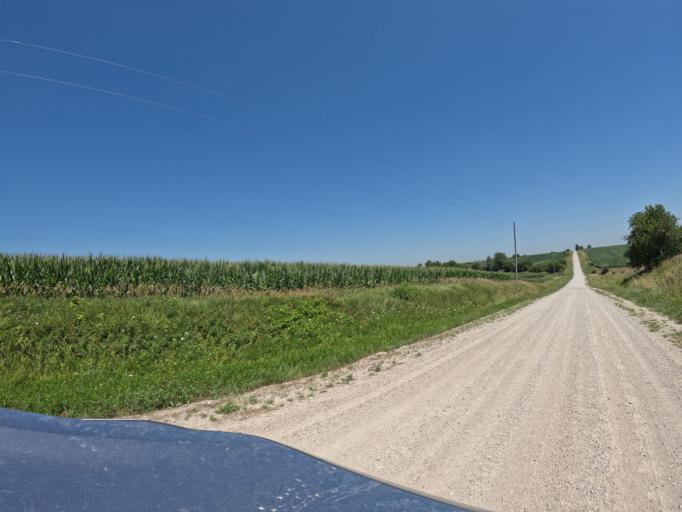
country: US
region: Iowa
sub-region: Keokuk County
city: Sigourney
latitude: 41.4235
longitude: -92.3431
